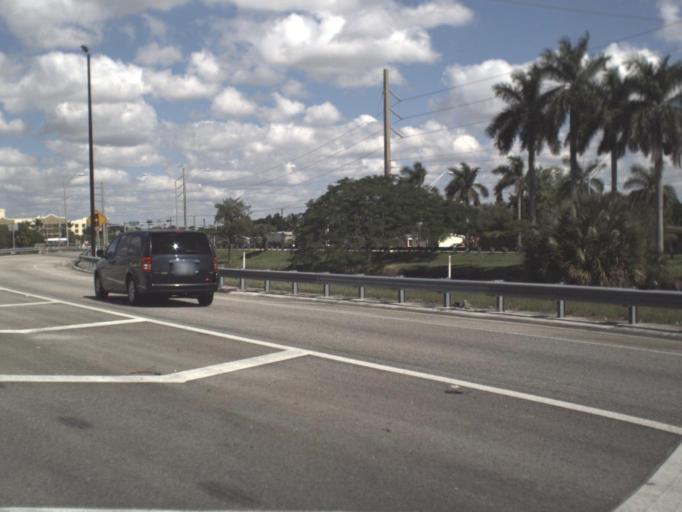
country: US
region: Florida
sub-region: Miami-Dade County
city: Westwood Lake
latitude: 25.7284
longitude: -80.3839
